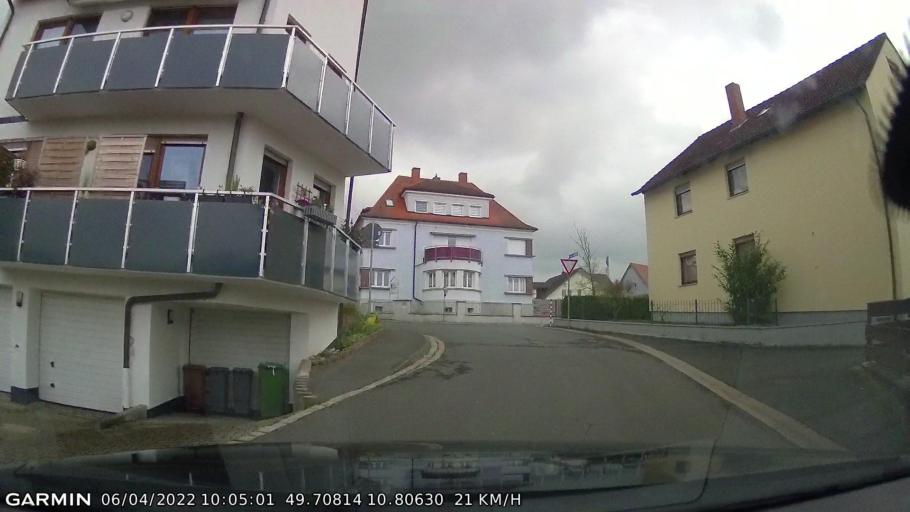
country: DE
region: Bavaria
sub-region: Regierungsbezirk Mittelfranken
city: Hochstadt an der Aisch
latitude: 49.7081
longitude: 10.8063
